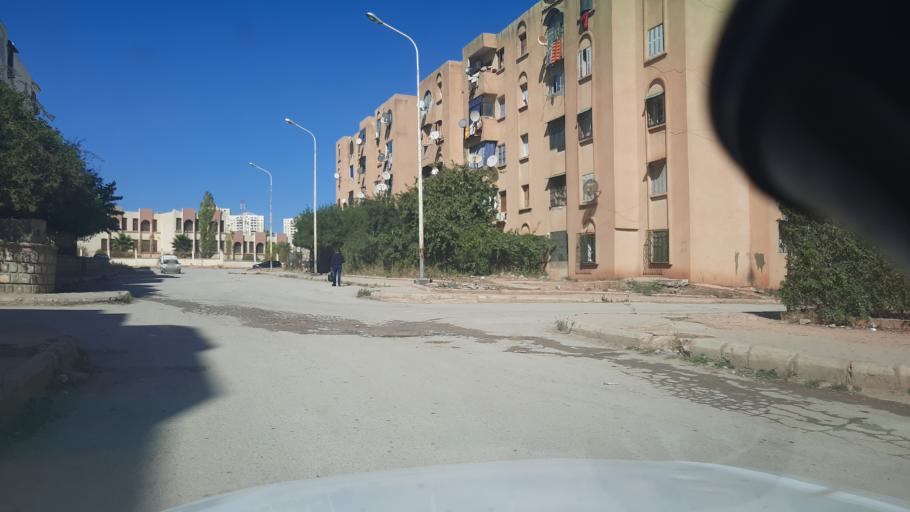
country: DZ
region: Constantine
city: Ain Smara
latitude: 36.2495
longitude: 6.5826
